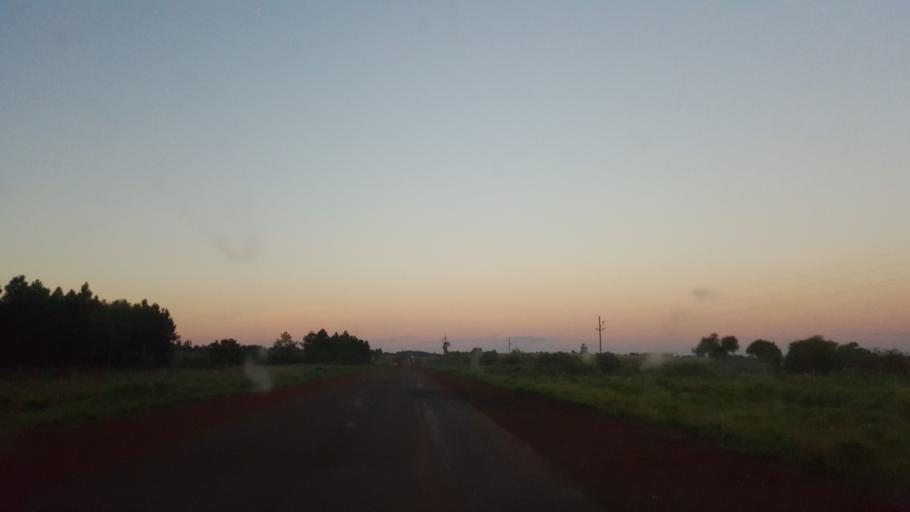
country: AR
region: Corrientes
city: Garruchos
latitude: -28.2184
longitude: -55.7956
